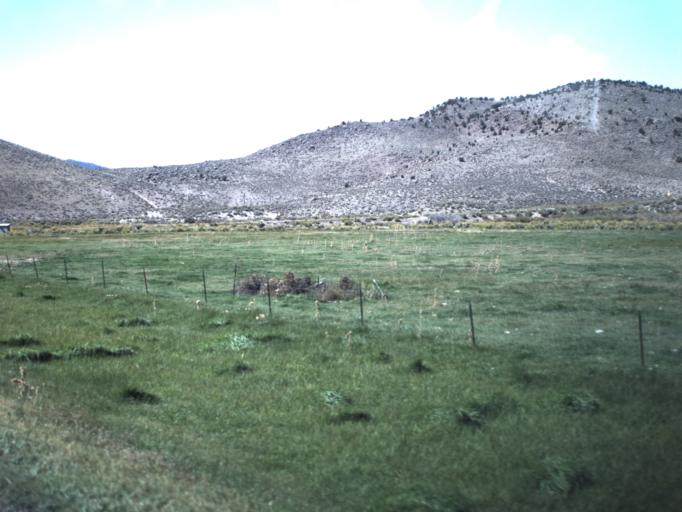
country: US
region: Utah
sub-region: Piute County
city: Junction
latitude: 38.1669
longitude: -112.0241
